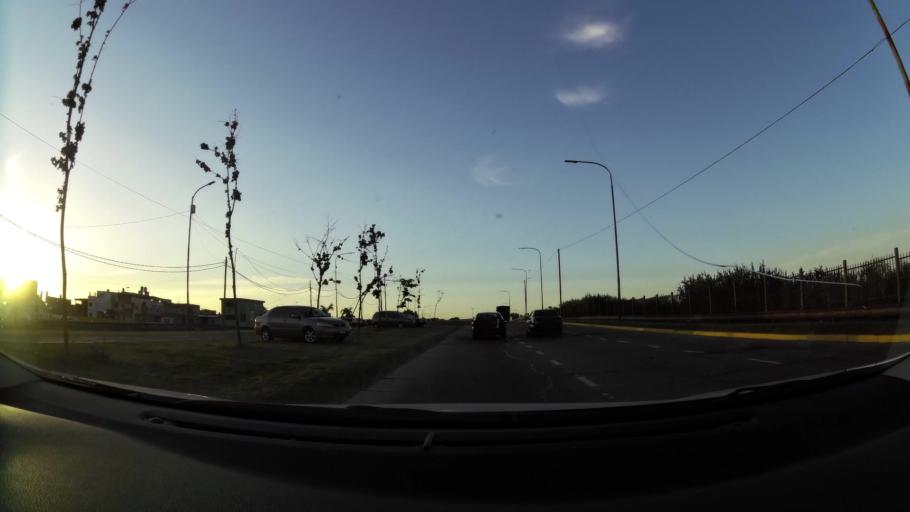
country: AR
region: Buenos Aires F.D.
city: Villa Lugano
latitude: -34.6717
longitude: -58.4609
